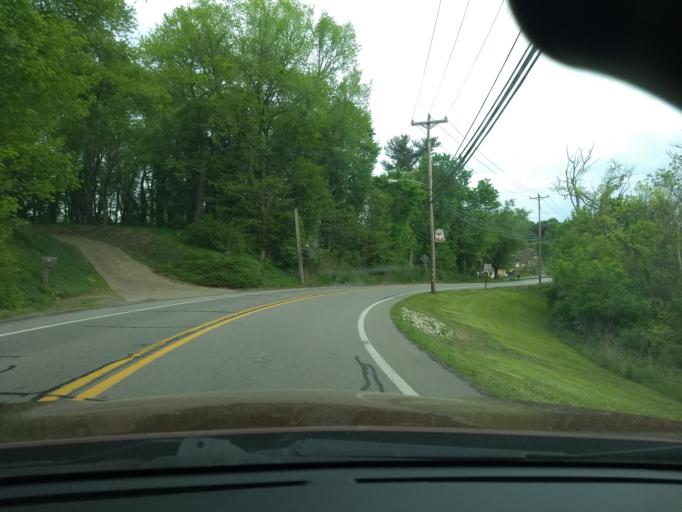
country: US
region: Pennsylvania
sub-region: Allegheny County
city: Rennerdale
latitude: 40.4562
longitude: -80.1373
